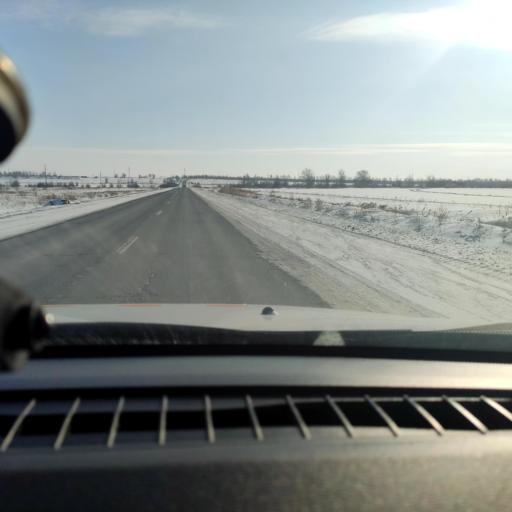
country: RU
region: Samara
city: Smyshlyayevka
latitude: 53.1631
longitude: 50.4570
